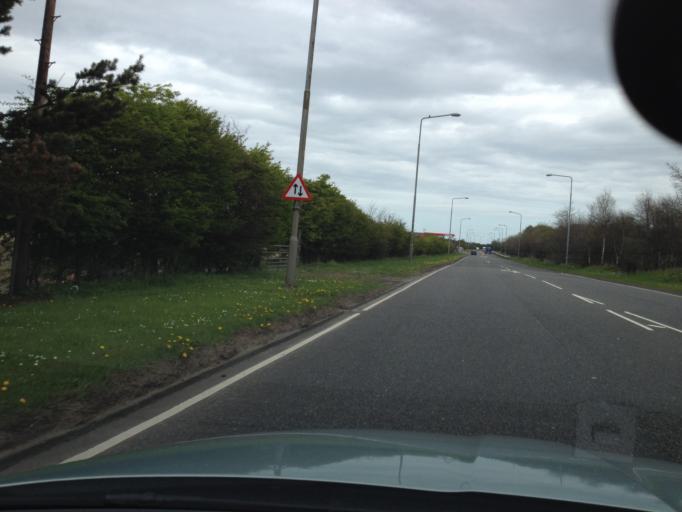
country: GB
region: Scotland
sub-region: West Lothian
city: Livingston
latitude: 55.9088
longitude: -3.5753
